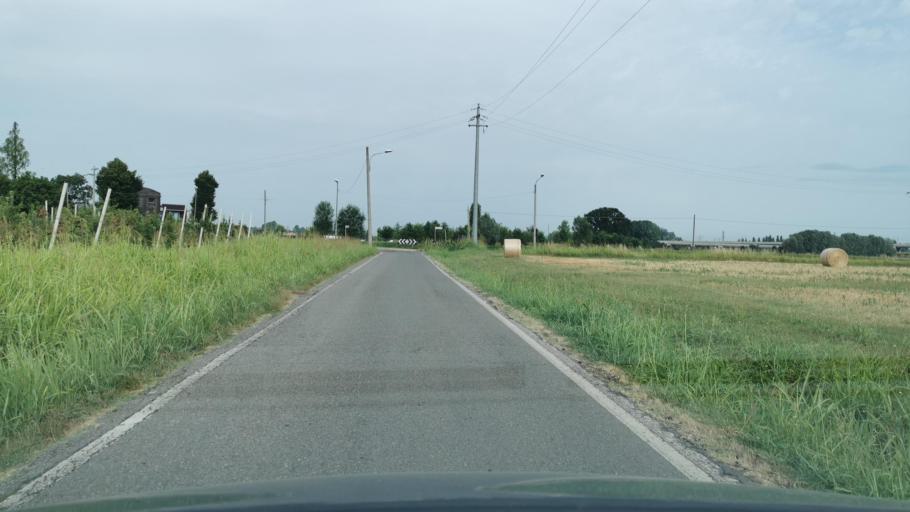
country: IT
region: Emilia-Romagna
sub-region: Provincia di Modena
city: Villanova
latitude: 44.6881
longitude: 10.8999
